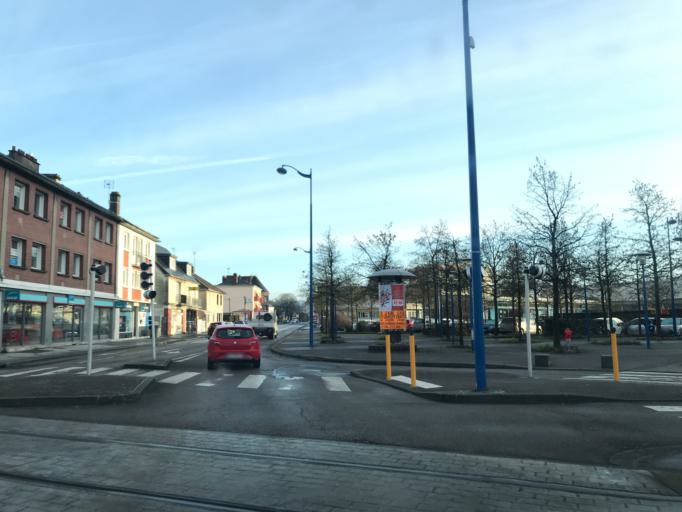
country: FR
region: Haute-Normandie
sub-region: Departement de la Seine-Maritime
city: Sotteville-les-Rouen
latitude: 49.4192
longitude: 1.0905
